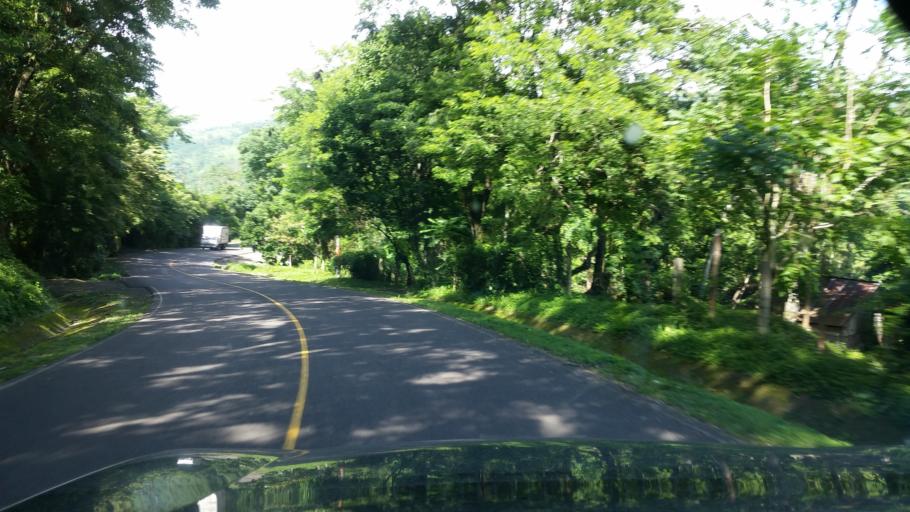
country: NI
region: Matagalpa
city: San Ramon
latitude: 13.0220
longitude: -85.7879
